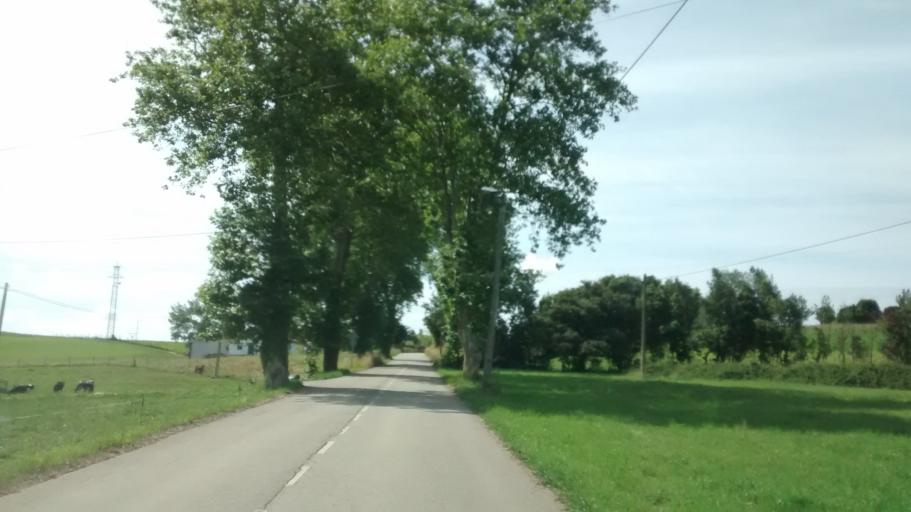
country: ES
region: Cantabria
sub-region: Provincia de Cantabria
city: Lierganes
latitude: 43.4052
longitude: -3.7395
